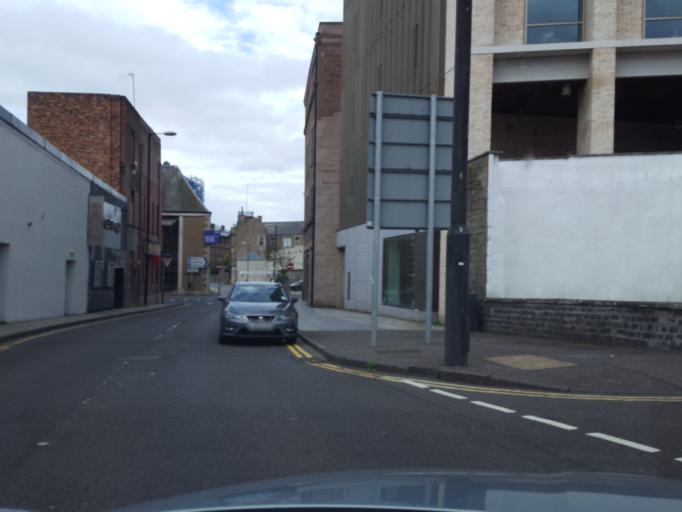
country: GB
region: Scotland
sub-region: Dundee City
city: Dundee
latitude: 56.4603
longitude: -2.9763
